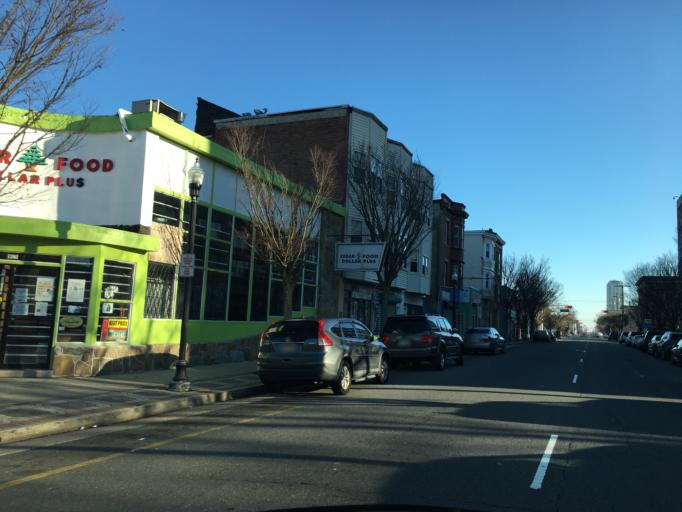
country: US
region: New Jersey
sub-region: Atlantic County
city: Atlantic City
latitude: 39.3653
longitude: -74.4252
